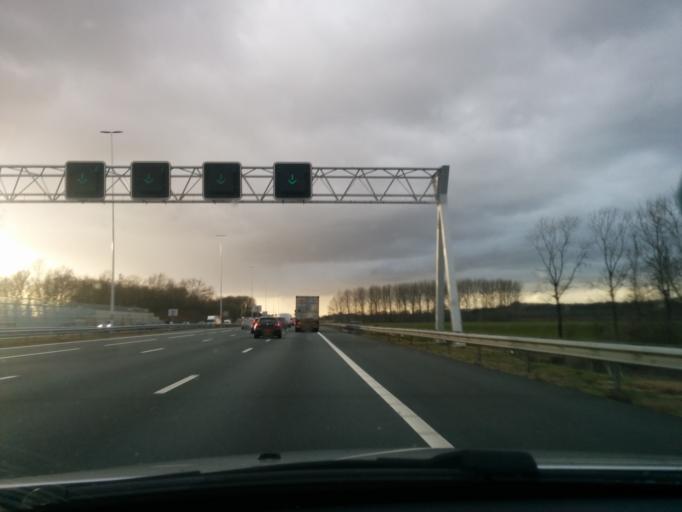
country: NL
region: Utrecht
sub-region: Gemeente Zeist
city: Zeist
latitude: 52.0586
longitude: 5.2429
